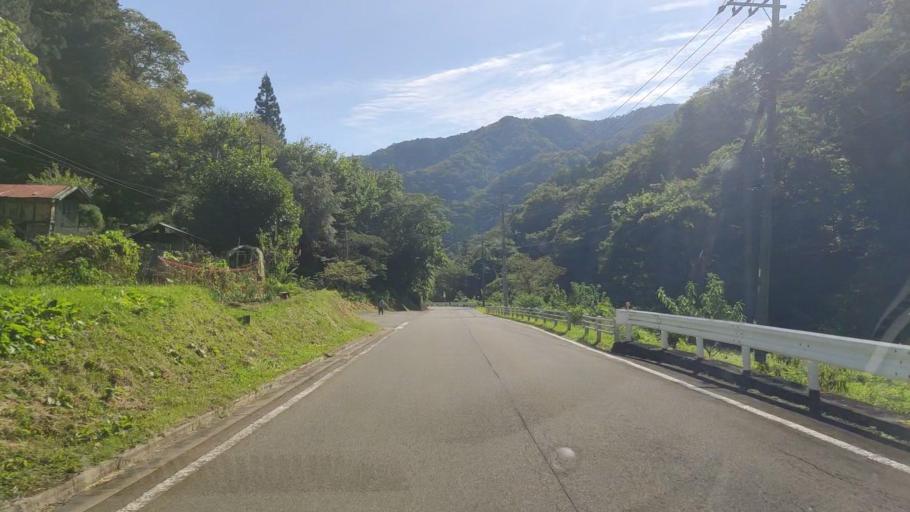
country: JP
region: Gunma
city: Nakanojomachi
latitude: 36.6000
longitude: 138.7056
